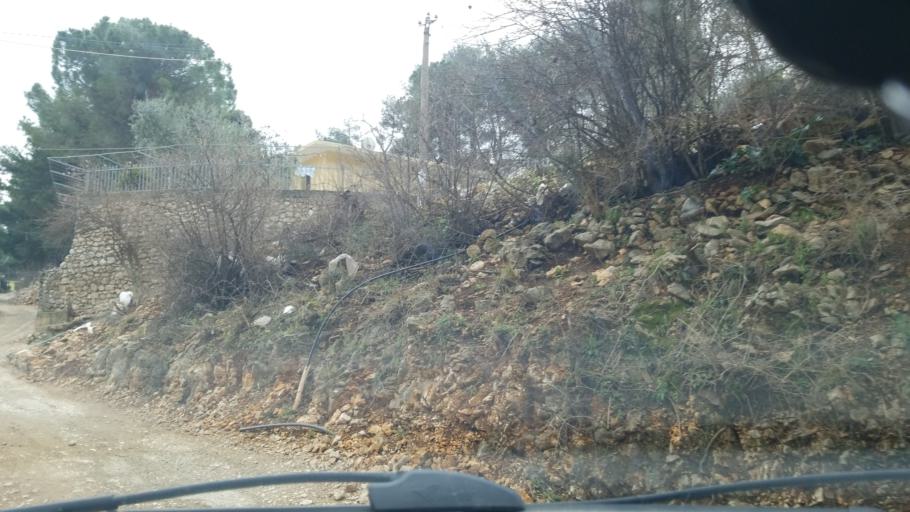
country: AL
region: Lezhe
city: Shengjin
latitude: 41.8165
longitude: 19.5836
